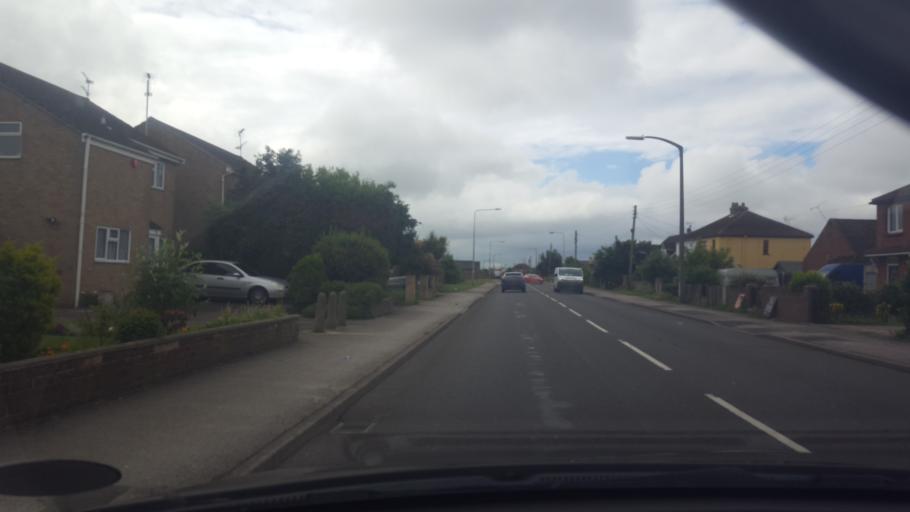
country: GB
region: England
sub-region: Essex
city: Little Clacton
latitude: 51.8005
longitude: 1.1181
